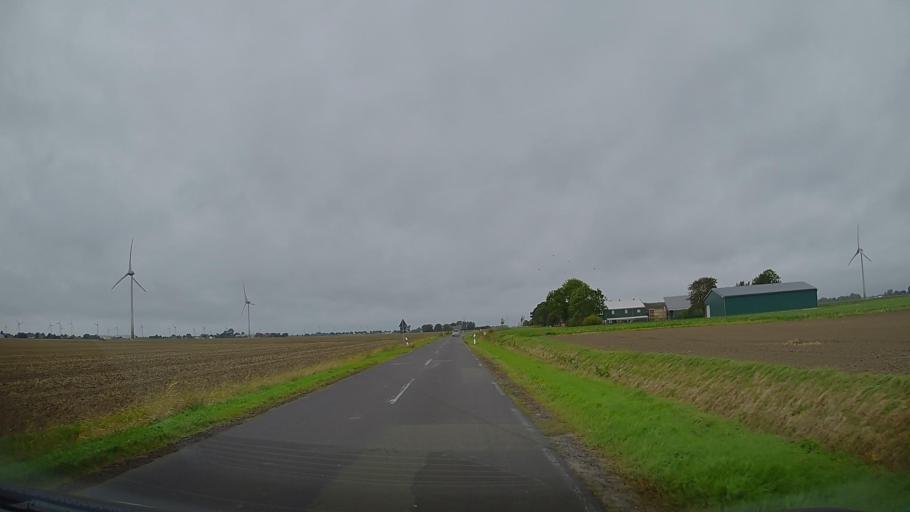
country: DE
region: Schleswig-Holstein
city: Marnerdeich
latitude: 53.9211
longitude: 8.9893
